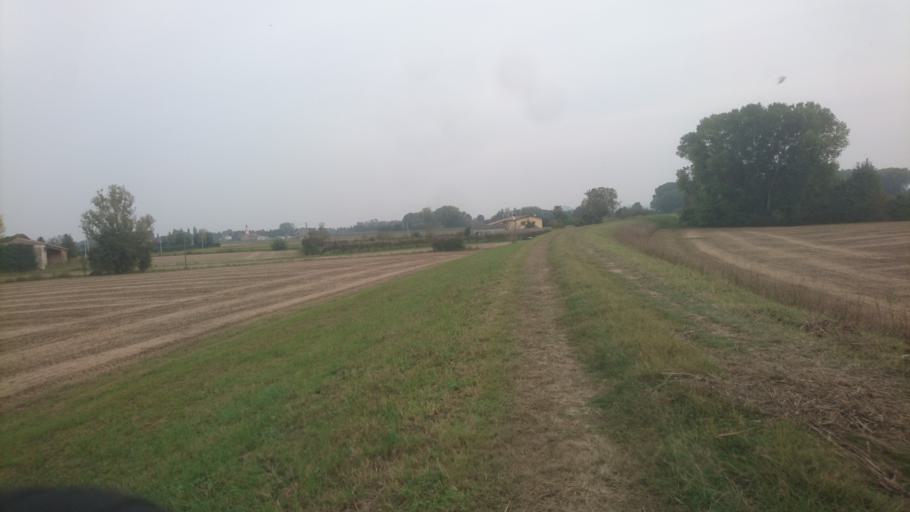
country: IT
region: Veneto
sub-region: Provincia di Padova
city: Cervarese Santa Croce
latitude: 45.4211
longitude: 11.7089
